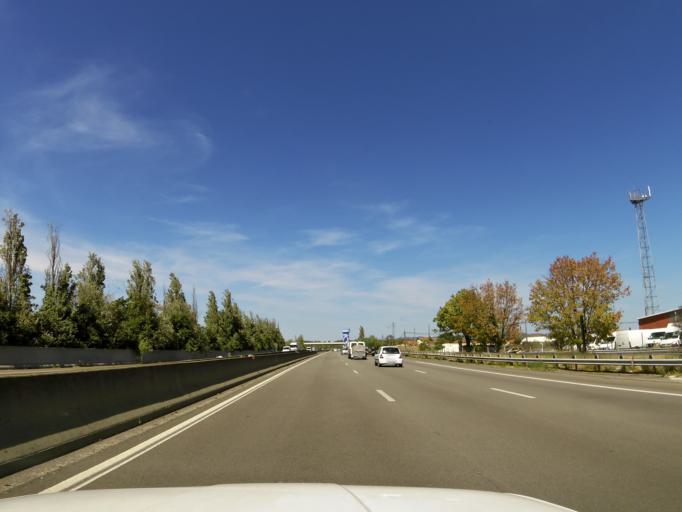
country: FR
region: Rhone-Alpes
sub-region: Departement de l'Isere
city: Chanas
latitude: 45.2871
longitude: 4.8221
